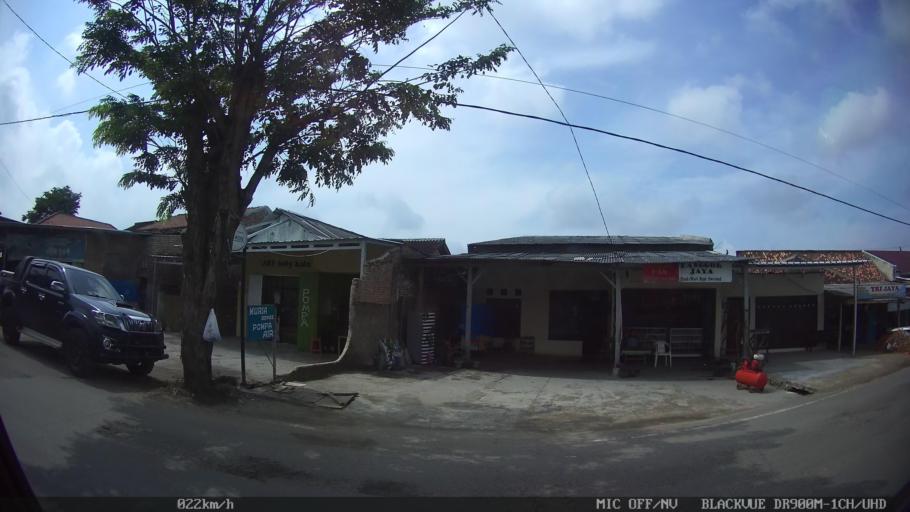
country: ID
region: Lampung
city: Kedaton
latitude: -5.3620
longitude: 105.2805
